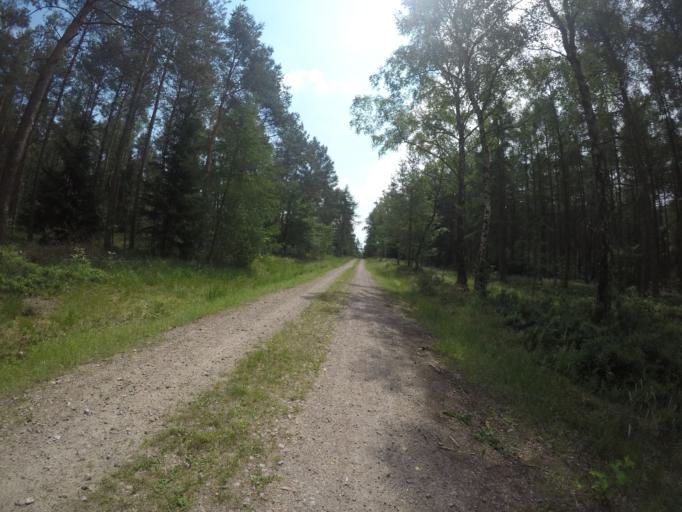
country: DE
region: Lower Saxony
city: Jesteburg
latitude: 53.2617
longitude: 9.9321
